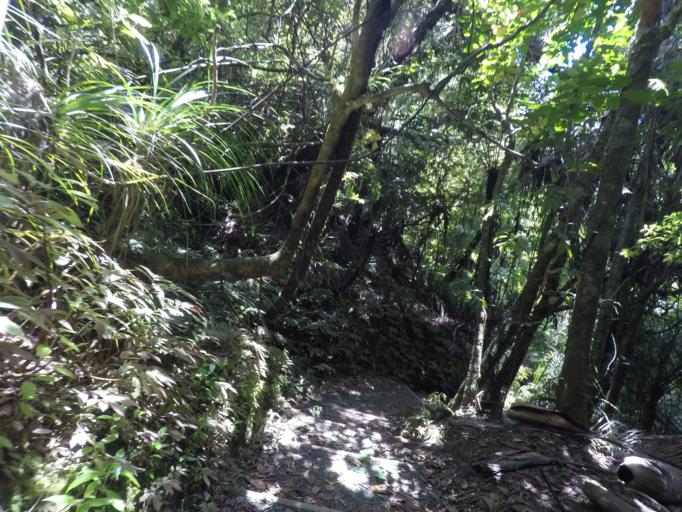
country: NZ
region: Auckland
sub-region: Auckland
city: Warkworth
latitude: -36.4550
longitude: 174.6509
